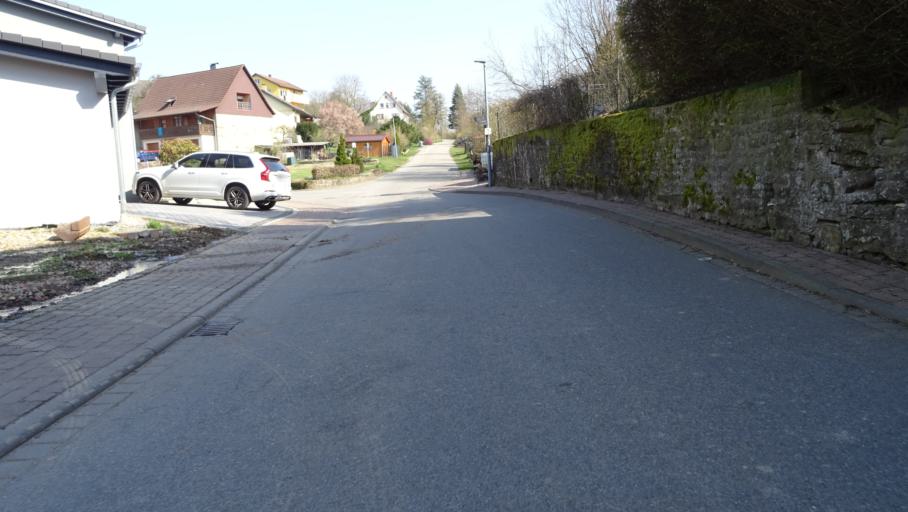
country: DE
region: Baden-Wuerttemberg
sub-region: Karlsruhe Region
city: Billigheim
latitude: 49.3996
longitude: 9.2810
